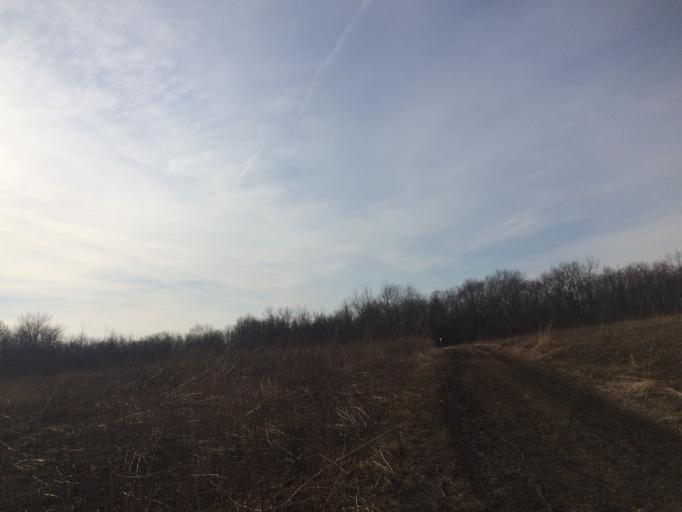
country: US
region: Illinois
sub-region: Cook County
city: Streamwood
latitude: 42.0588
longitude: -88.2024
